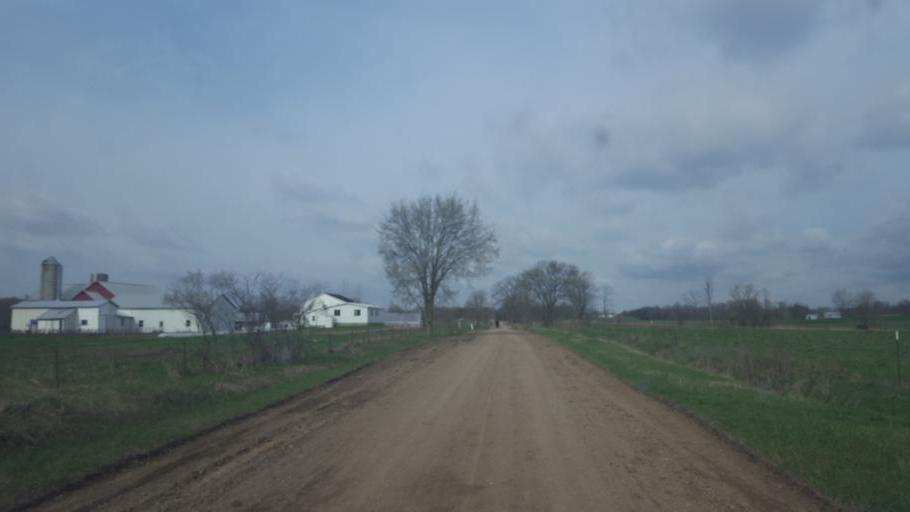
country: US
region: Michigan
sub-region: Montcalm County
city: Edmore
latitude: 43.4809
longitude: -84.9493
